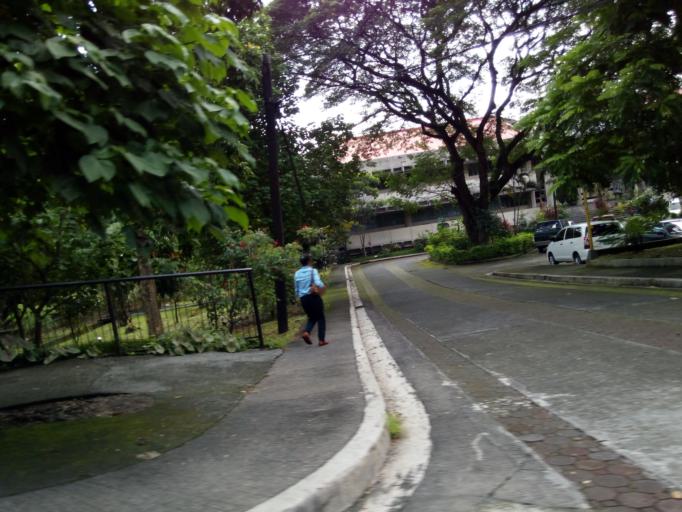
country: PH
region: Metro Manila
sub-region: Quezon City
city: Quezon City
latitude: 14.6508
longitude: 121.0685
